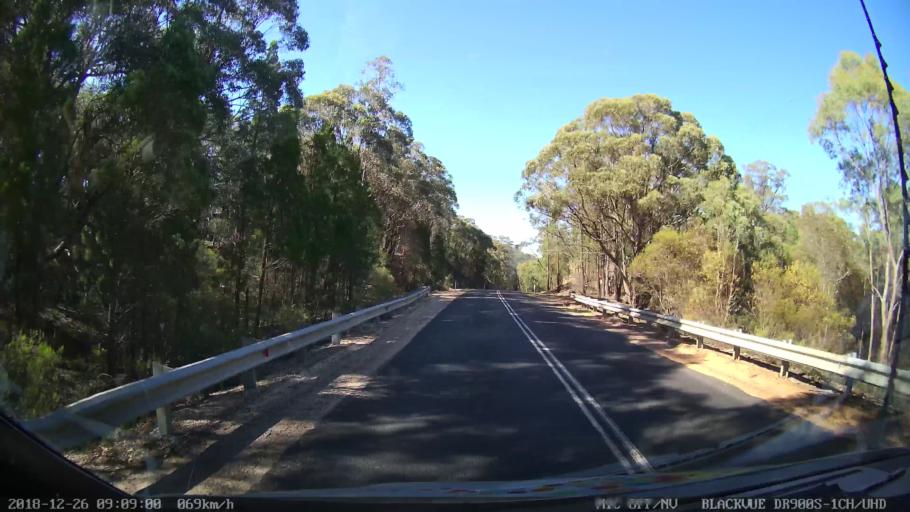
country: AU
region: New South Wales
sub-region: Mid-Western Regional
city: Kandos
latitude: -32.7208
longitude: 149.9993
